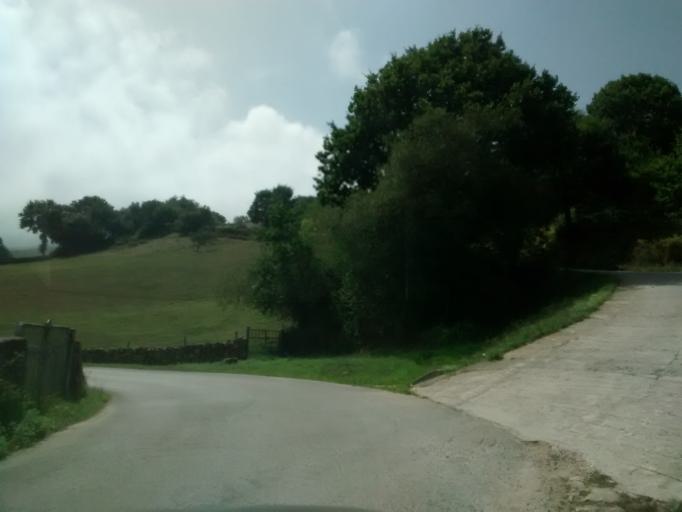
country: ES
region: Cantabria
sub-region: Provincia de Cantabria
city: Ruente
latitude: 43.2549
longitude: -4.2466
